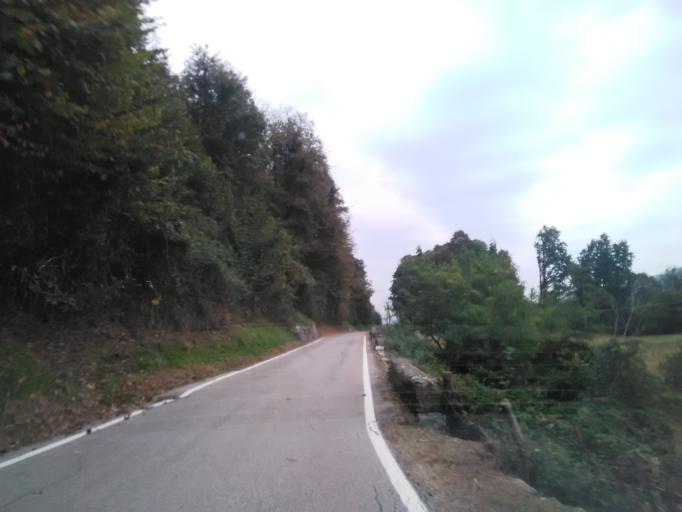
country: IT
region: Piedmont
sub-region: Provincia di Vercelli
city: Quarona
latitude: 45.7461
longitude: 8.2558
